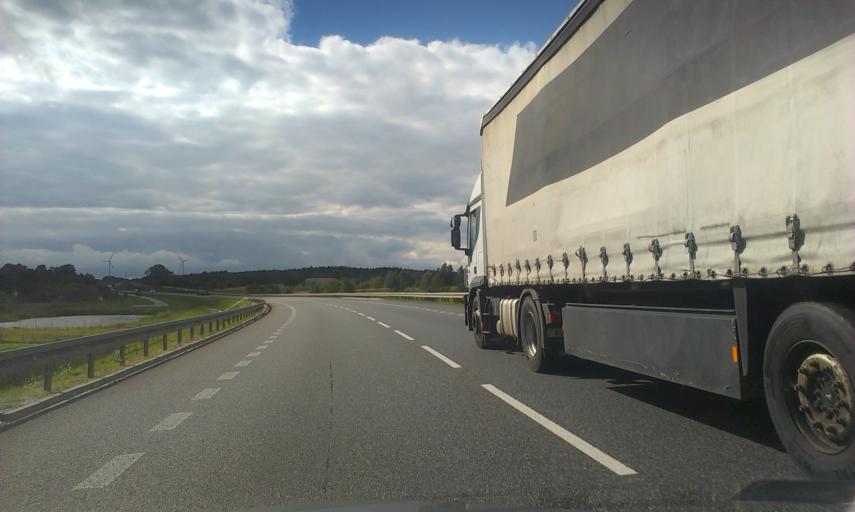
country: PL
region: Masovian Voivodeship
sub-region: Powiat zyrardowski
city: Radziejowice
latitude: 51.9768
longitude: 20.5677
